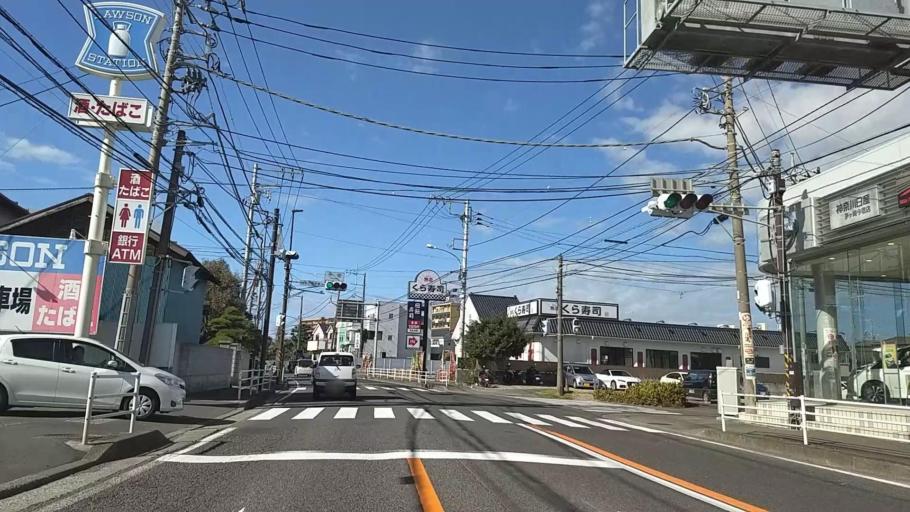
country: JP
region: Kanagawa
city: Chigasaki
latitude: 35.3331
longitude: 139.3822
